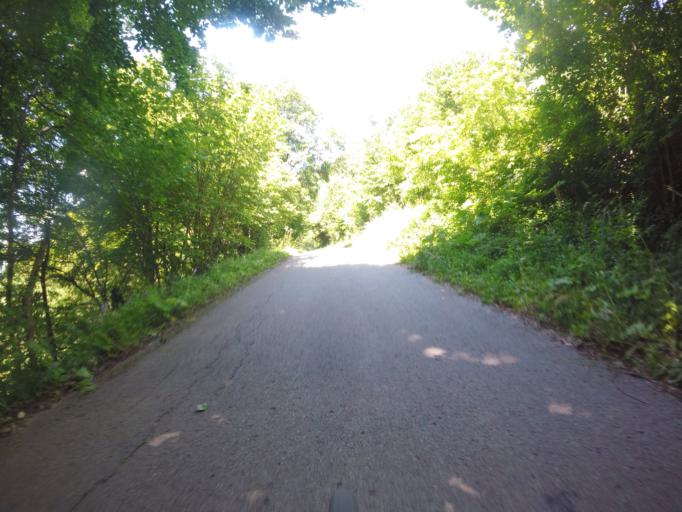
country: SI
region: Kostanjevica na Krki
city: Kostanjevica na Krki
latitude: 45.7616
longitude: 15.4467
